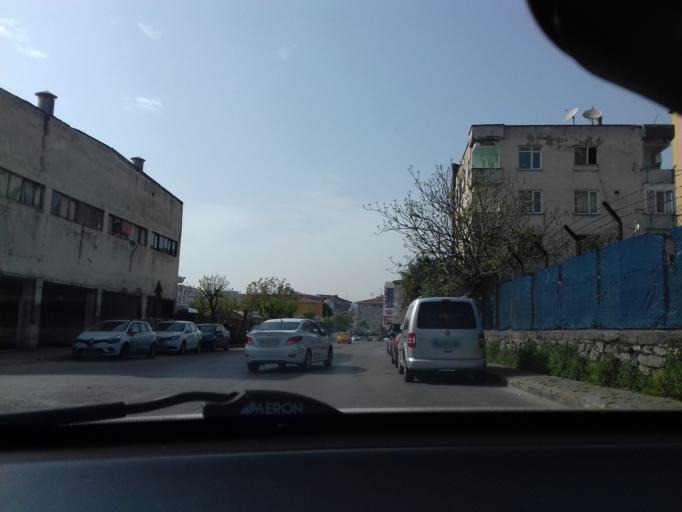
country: TR
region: Istanbul
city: Maltepe
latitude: 40.9141
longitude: 29.2085
